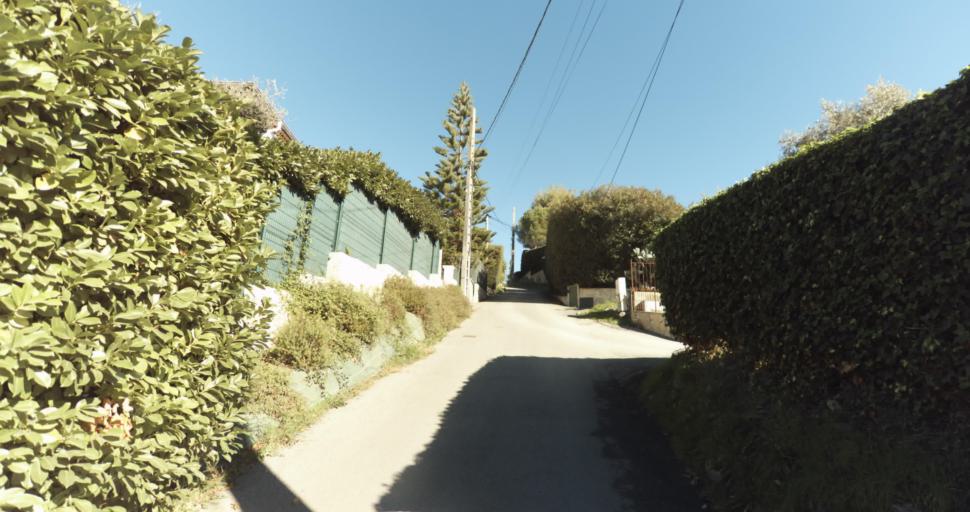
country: FR
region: Provence-Alpes-Cote d'Azur
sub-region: Departement des Alpes-Maritimes
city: Saint-Paul-de-Vence
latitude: 43.7101
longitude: 7.1235
